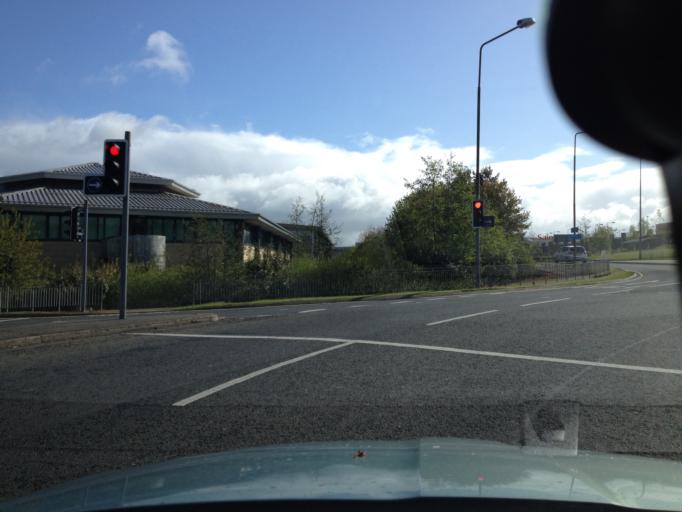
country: GB
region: Scotland
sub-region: West Lothian
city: Livingston
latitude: 55.8784
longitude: -3.5285
